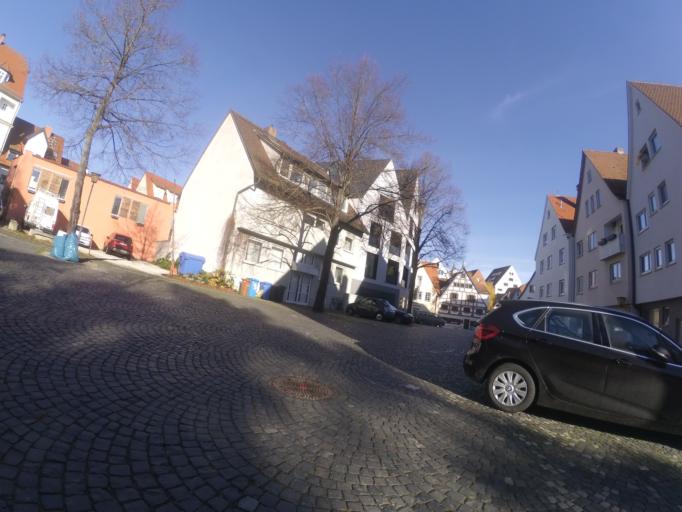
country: DE
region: Baden-Wuerttemberg
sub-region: Tuebingen Region
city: Ulm
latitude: 48.3948
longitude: 9.9897
